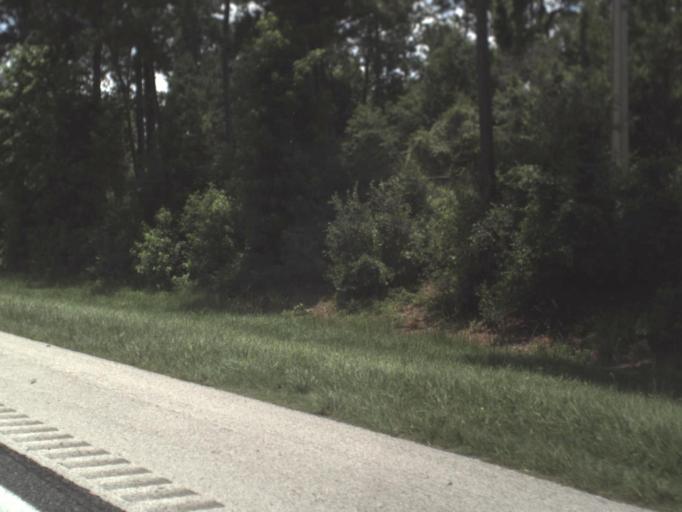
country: US
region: Florida
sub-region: Alachua County
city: Alachua
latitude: 29.7050
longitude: -82.4601
